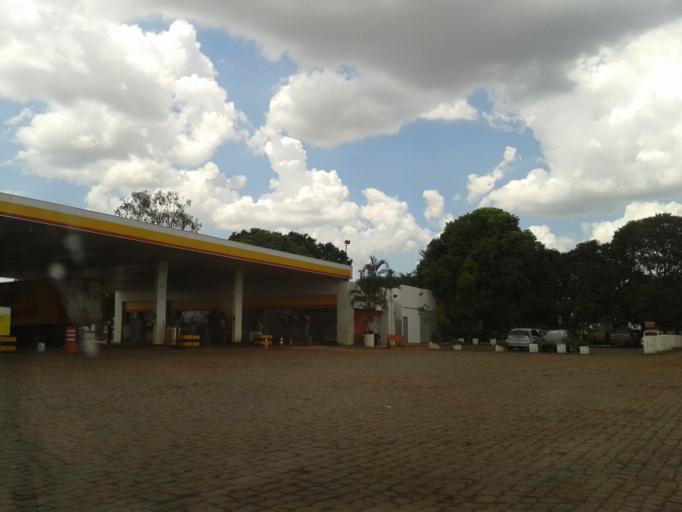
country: BR
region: Goias
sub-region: Itumbiara
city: Itumbiara
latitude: -18.3822
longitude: -49.2081
